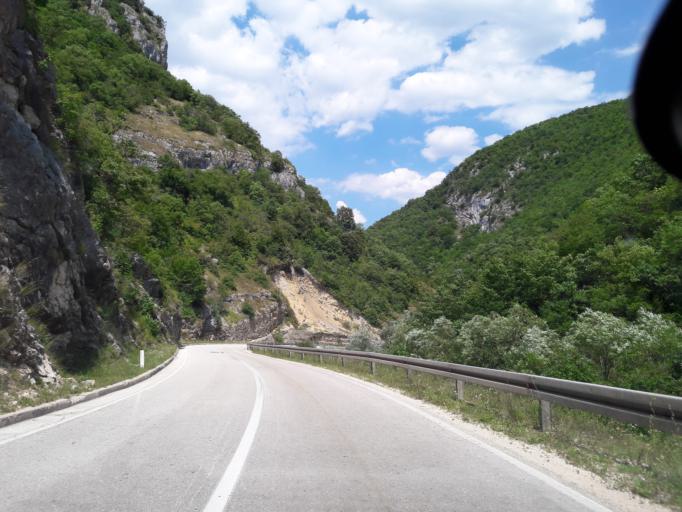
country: BA
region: Republika Srpska
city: Mrkonjic Grad
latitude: 44.4584
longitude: 17.1604
